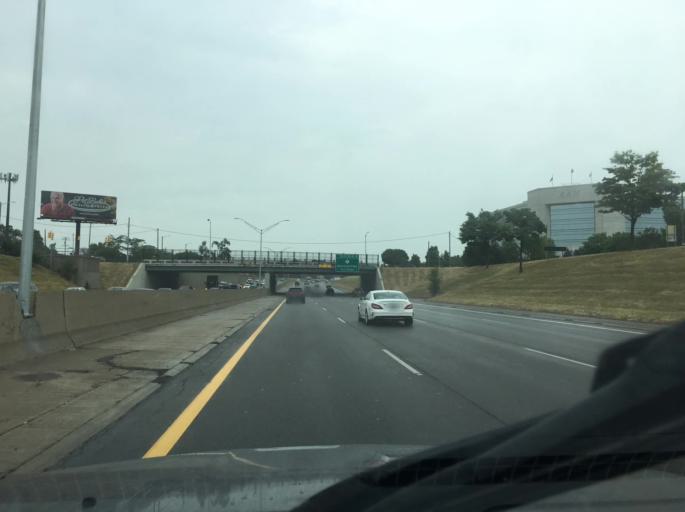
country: US
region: Michigan
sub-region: Wayne County
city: Hamtramck
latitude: 42.3854
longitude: -83.0674
